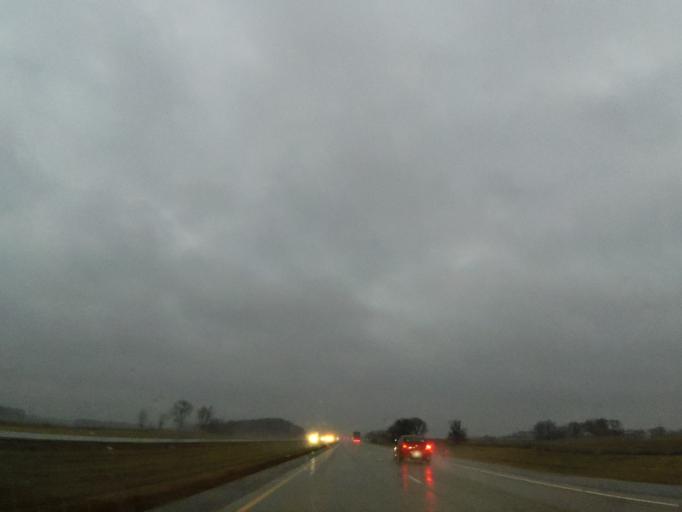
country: US
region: Minnesota
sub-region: Freeborn County
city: Albert Lea
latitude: 43.5583
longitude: -93.3590
